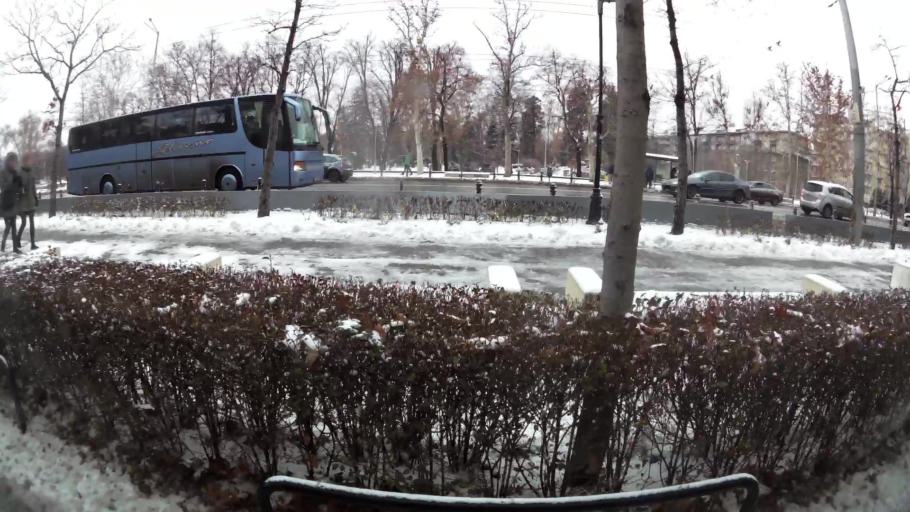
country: BG
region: Sofia-Capital
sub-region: Stolichna Obshtina
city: Sofia
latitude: 42.6924
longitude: 23.3355
